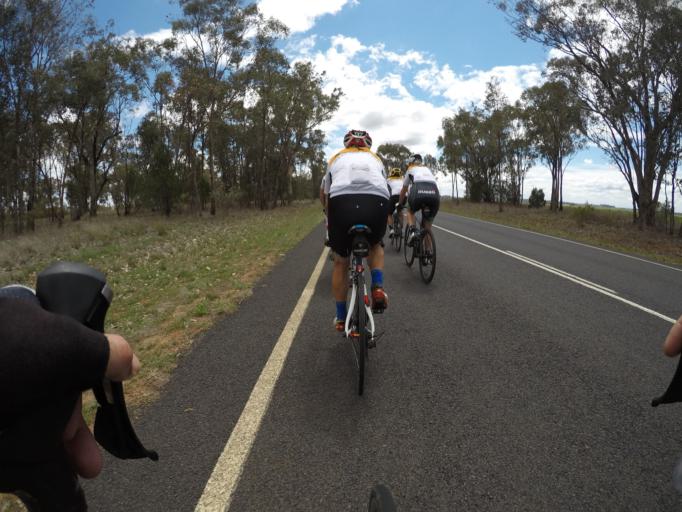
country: AU
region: New South Wales
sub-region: Dubbo Municipality
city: Dubbo
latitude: -32.4088
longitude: 148.5710
